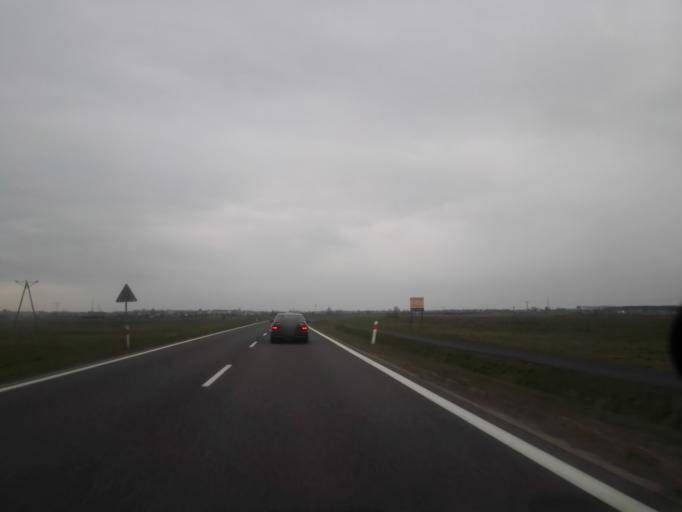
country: PL
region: Podlasie
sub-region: Powiat grajewski
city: Grajewo
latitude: 53.6573
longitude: 22.5014
